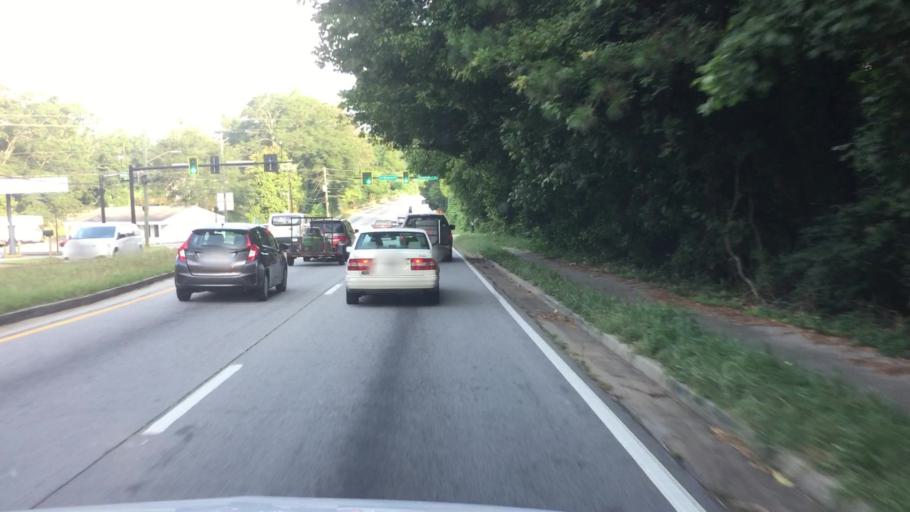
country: US
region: Georgia
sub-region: DeKalb County
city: Panthersville
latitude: 33.6828
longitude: -84.2456
